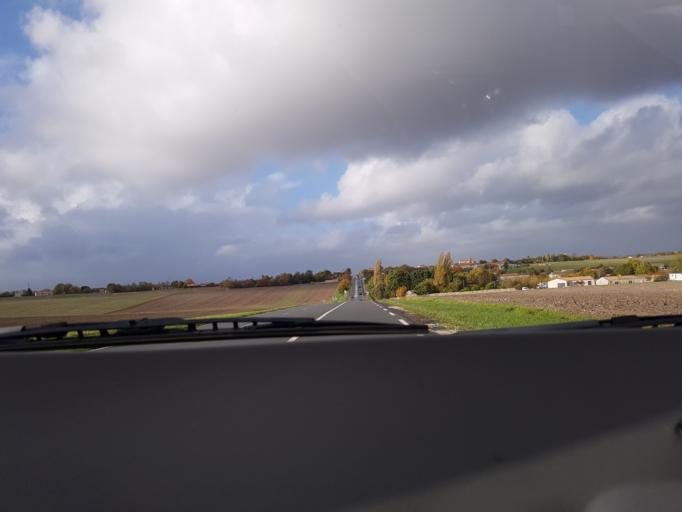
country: FR
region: Poitou-Charentes
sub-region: Departement de la Charente-Maritime
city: Thenac
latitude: 45.6472
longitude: -0.5838
